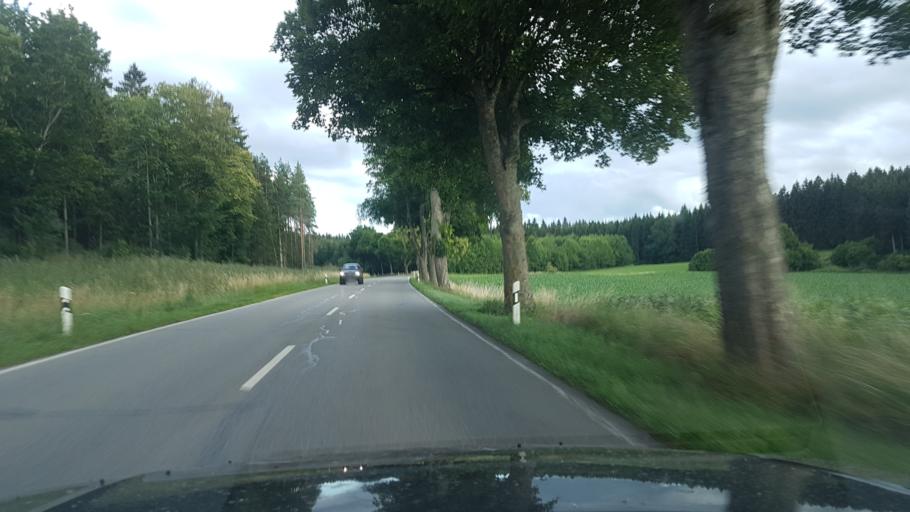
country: DE
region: Baden-Wuerttemberg
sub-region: Freiburg Region
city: Braunlingen
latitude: 47.9636
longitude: 8.4452
